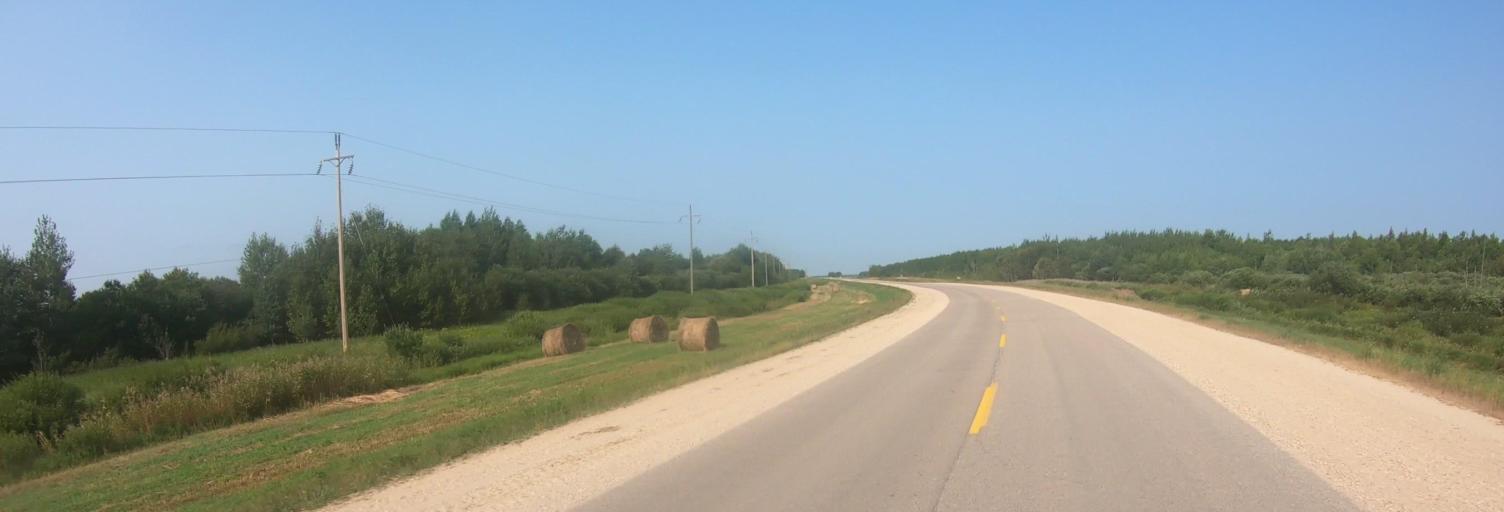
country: US
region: Minnesota
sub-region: Roseau County
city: Roseau
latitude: 49.0230
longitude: -95.5640
